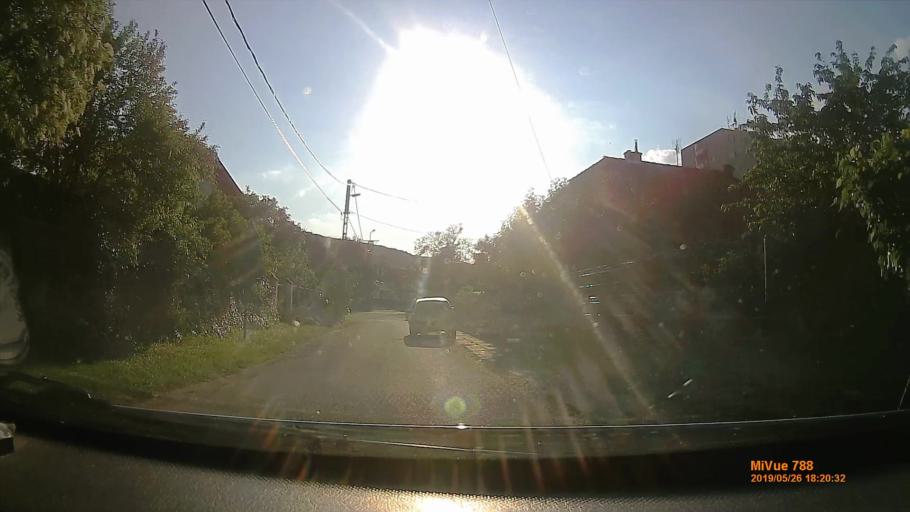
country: HU
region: Borsod-Abauj-Zemplen
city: Sajobabony
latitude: 48.1066
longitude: 20.6765
